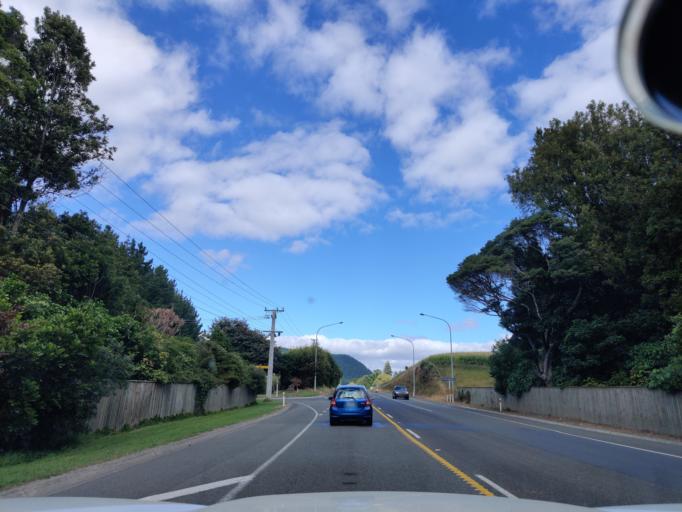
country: NZ
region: Wellington
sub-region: Kapiti Coast District
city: Otaki
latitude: -40.7277
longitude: 175.2078
